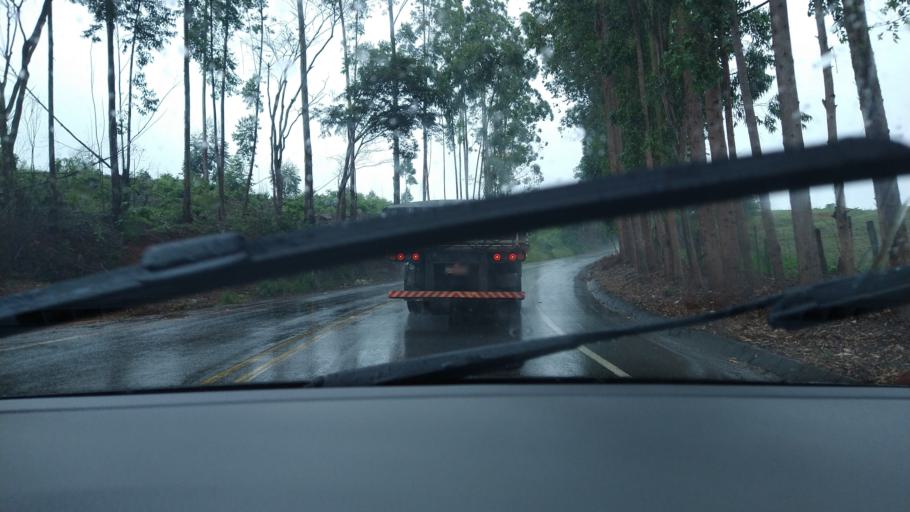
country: BR
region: Minas Gerais
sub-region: Ponte Nova
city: Ponte Nova
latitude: -20.5775
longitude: -42.8803
